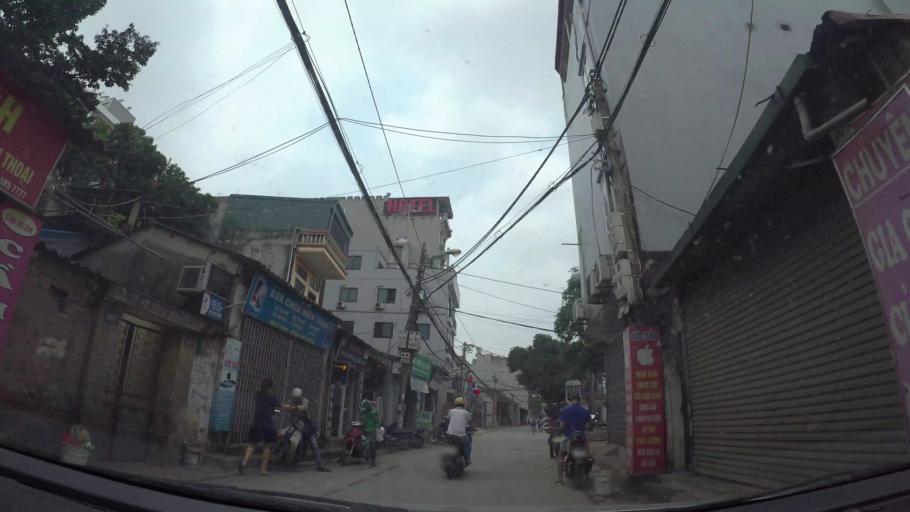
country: VN
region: Ha Noi
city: Tay Ho
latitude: 21.0719
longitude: 105.7898
